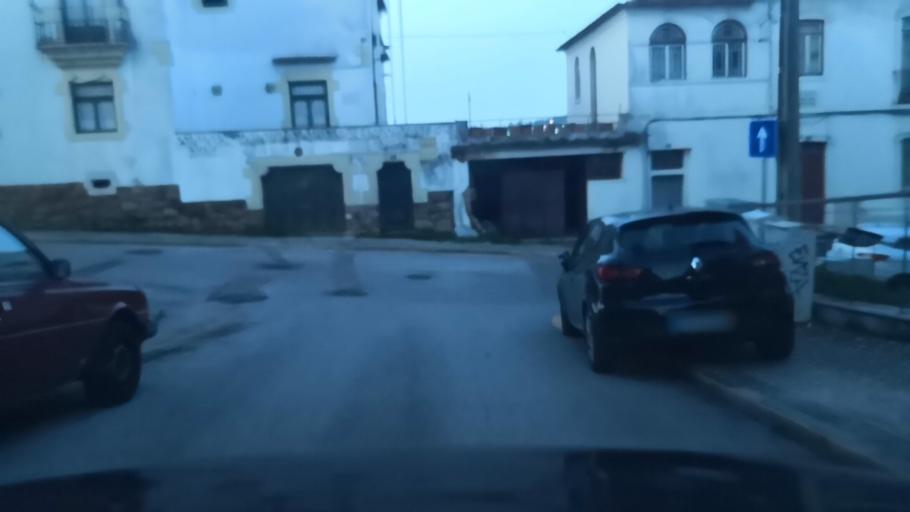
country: PT
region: Leiria
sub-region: Leiria
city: Leiria
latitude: 39.7423
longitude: -8.8064
